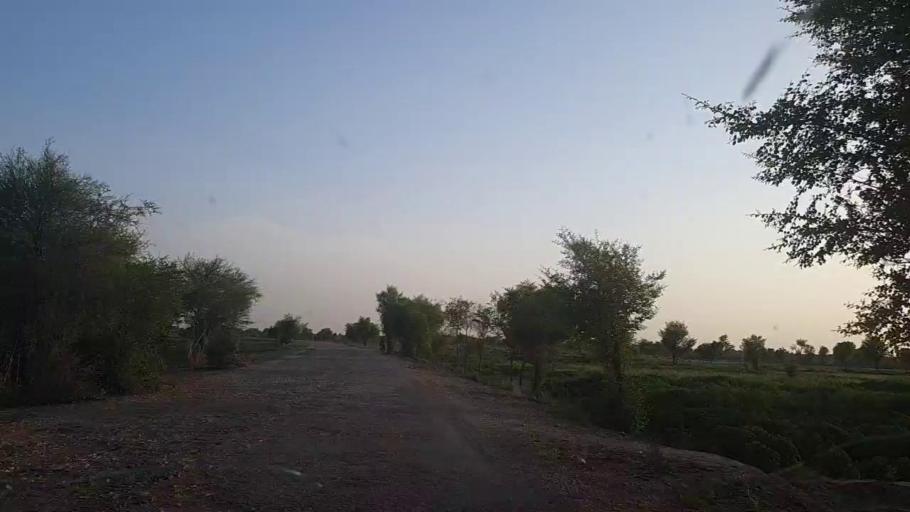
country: PK
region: Sindh
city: Khanpur
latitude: 27.6102
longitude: 69.4373
